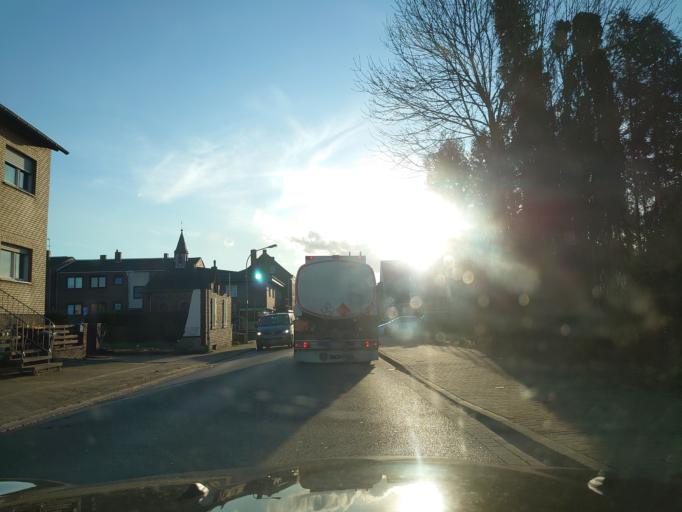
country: DE
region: North Rhine-Westphalia
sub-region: Regierungsbezirk Dusseldorf
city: Rommerskirchen
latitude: 51.0564
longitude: 6.7174
